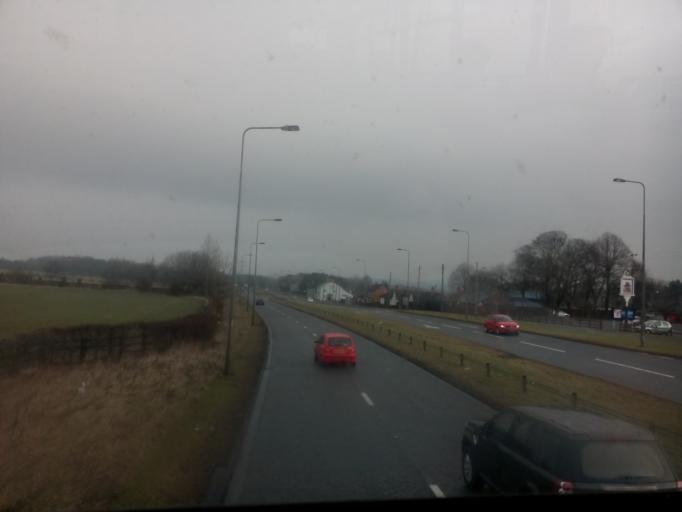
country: GB
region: England
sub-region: County Durham
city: Chester-le-Street
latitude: 54.8353
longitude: -1.5898
